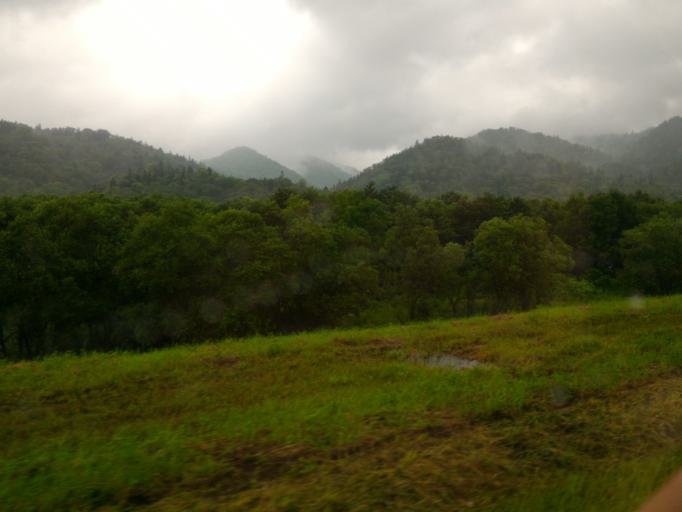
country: JP
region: Hokkaido
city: Nayoro
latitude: 44.7318
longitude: 142.2027
